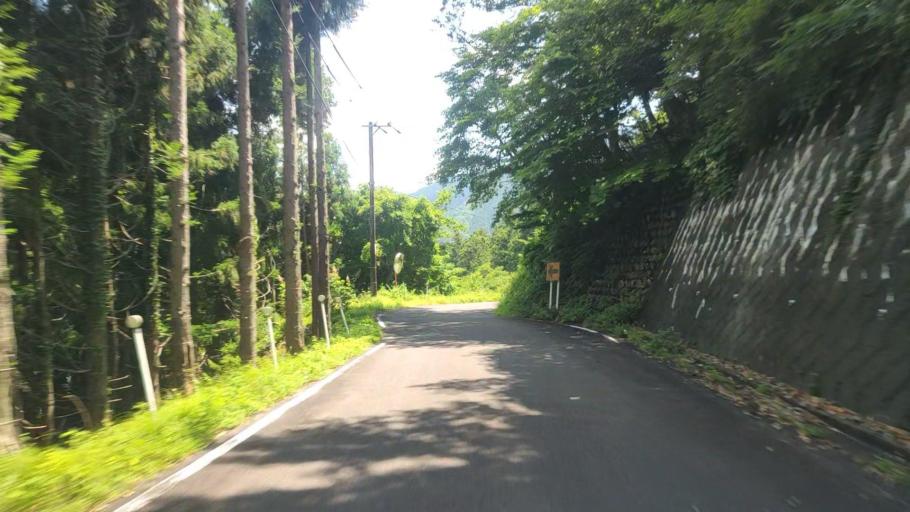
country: JP
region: Fukui
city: Ono
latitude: 35.7370
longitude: 136.5800
